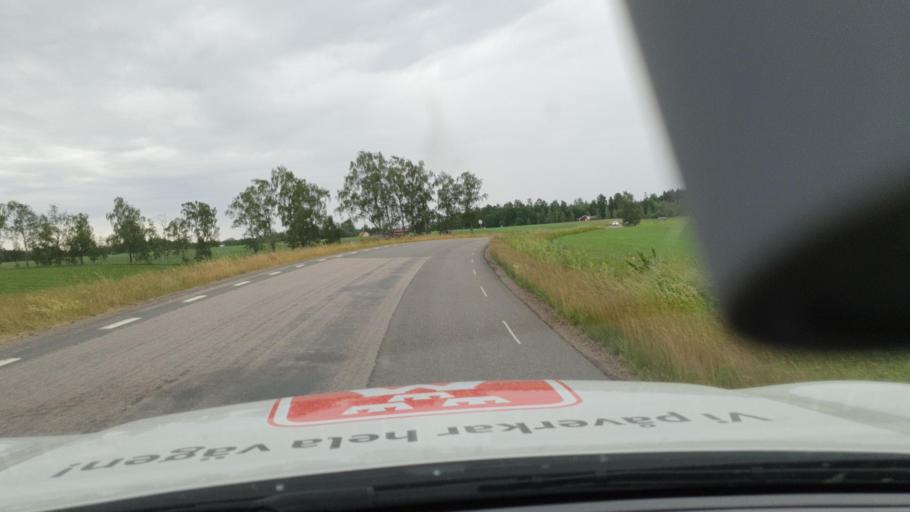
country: SE
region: Vaestra Goetaland
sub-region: Skovde Kommun
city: Skoevde
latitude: 58.3781
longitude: 13.9267
